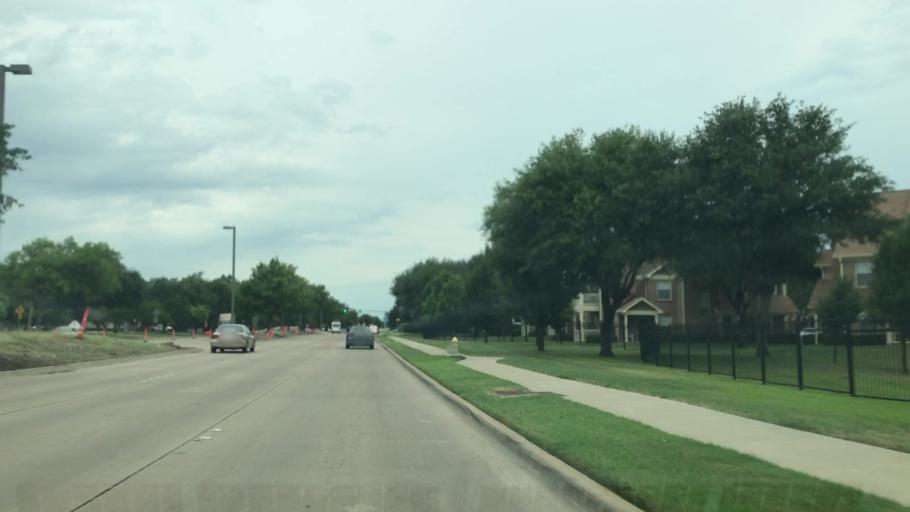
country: US
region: Texas
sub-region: Collin County
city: Plano
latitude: 32.9977
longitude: -96.7143
